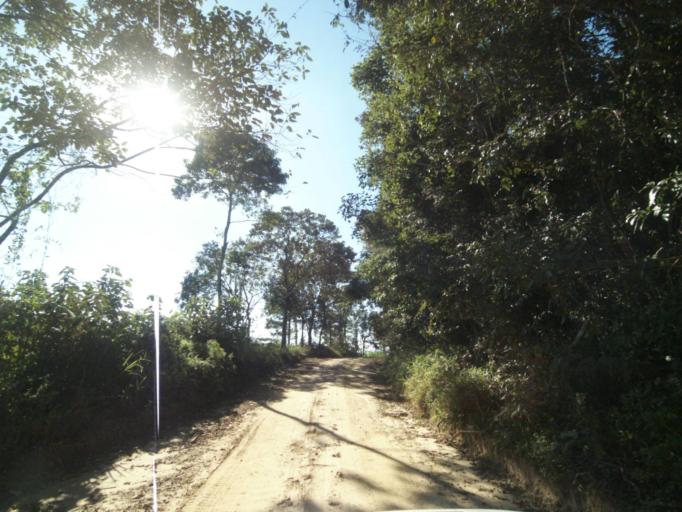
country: BR
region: Parana
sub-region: Tibagi
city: Tibagi
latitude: -24.5483
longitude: -50.4693
